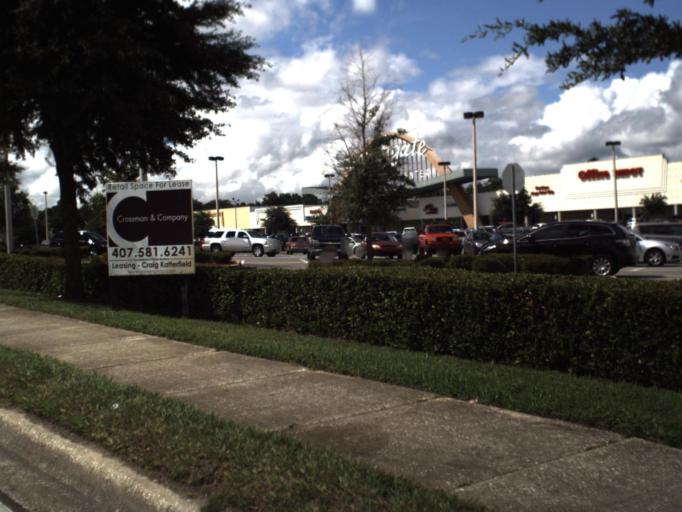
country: US
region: Florida
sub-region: Polk County
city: Lakeland
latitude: 28.0152
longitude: -81.9571
